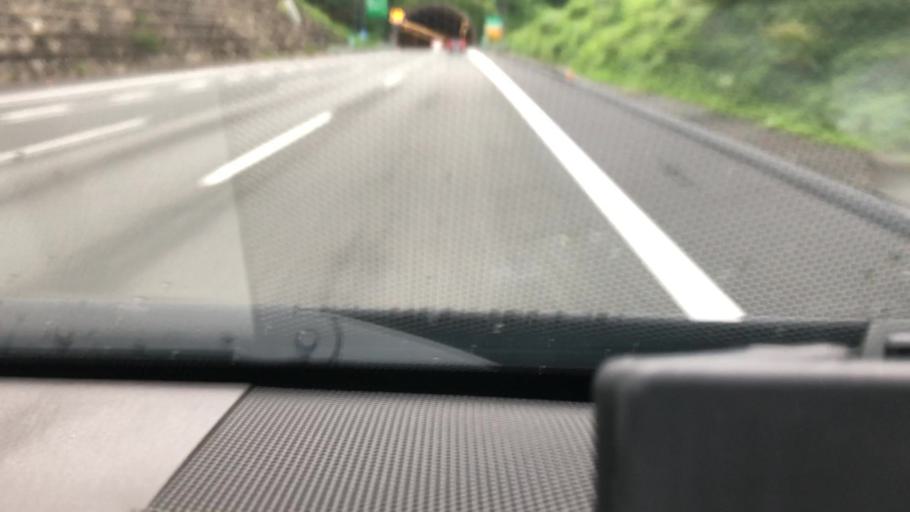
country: JP
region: Shizuoka
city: Kakegawa
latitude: 34.8419
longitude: 138.0479
